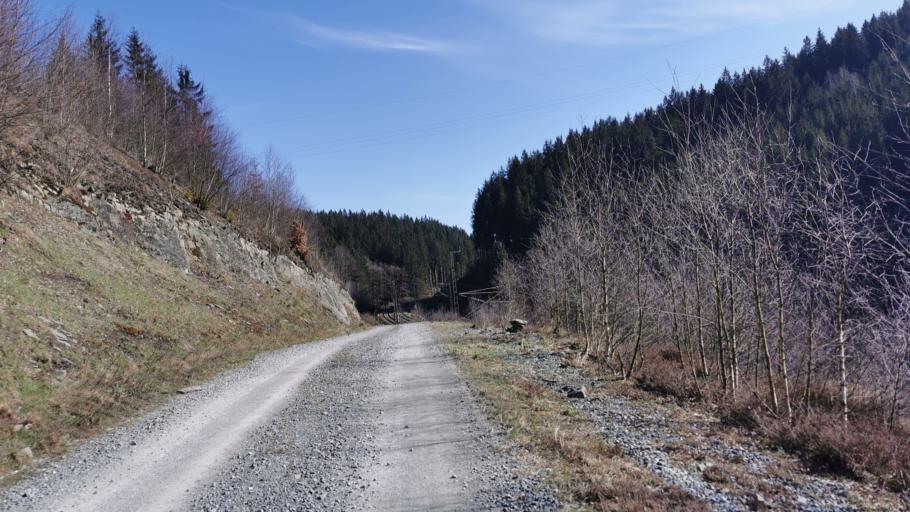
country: DE
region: Bavaria
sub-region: Upper Franconia
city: Teuschnitz
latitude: 50.4143
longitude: 11.3655
